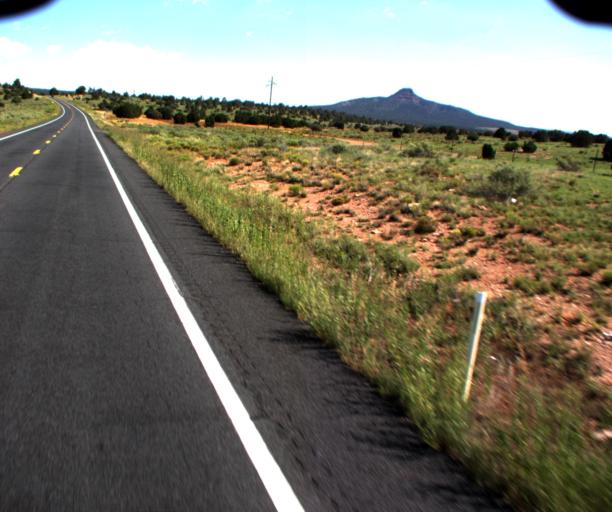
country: US
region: Arizona
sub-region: Coconino County
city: Grand Canyon Village
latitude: 35.7733
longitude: -112.1296
